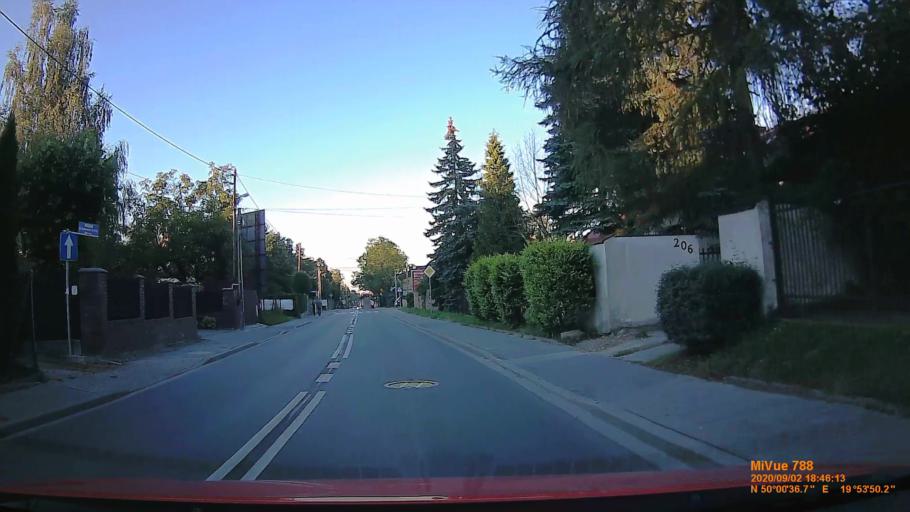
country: PL
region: Lesser Poland Voivodeship
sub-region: Krakow
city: Sidzina
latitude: 50.0104
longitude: 19.8975
